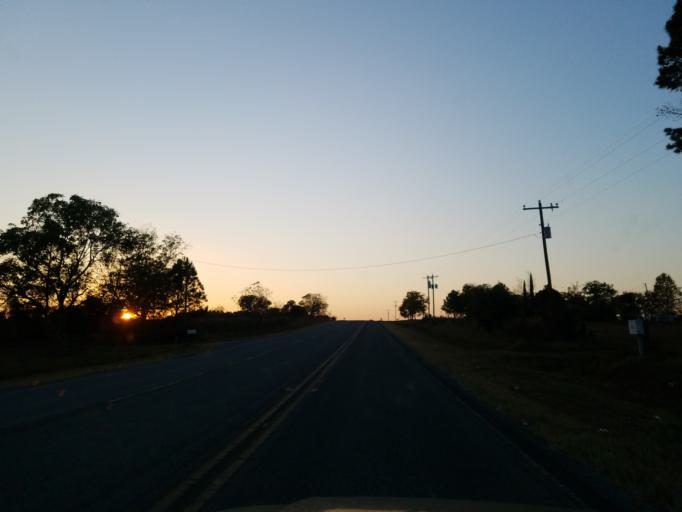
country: US
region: Georgia
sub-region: Ben Hill County
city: Fitzgerald
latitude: 31.7202
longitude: -83.4060
